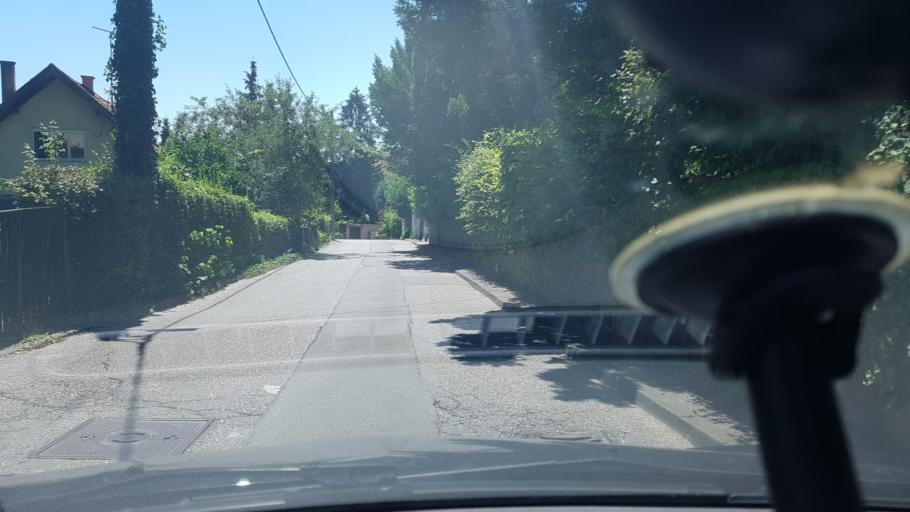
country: HR
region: Grad Zagreb
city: Zagreb
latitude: 45.8396
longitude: 15.9735
